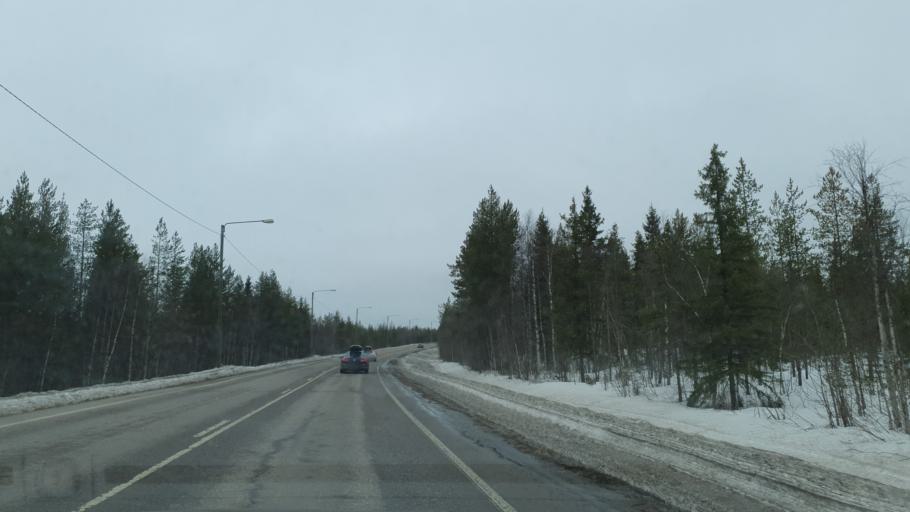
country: FI
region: Lapland
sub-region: Torniolaakso
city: Pello
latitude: 66.8270
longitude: 24.0019
